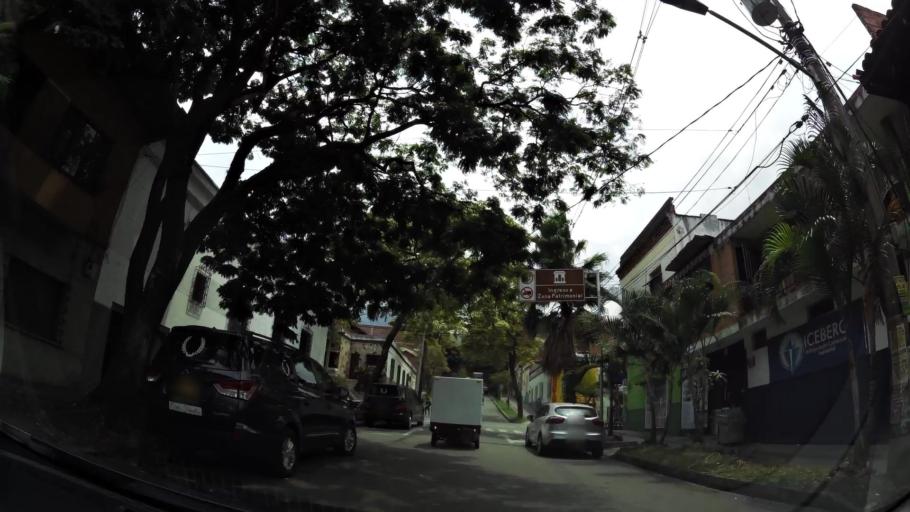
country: CO
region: Antioquia
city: Medellin
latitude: 6.2615
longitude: -75.5640
